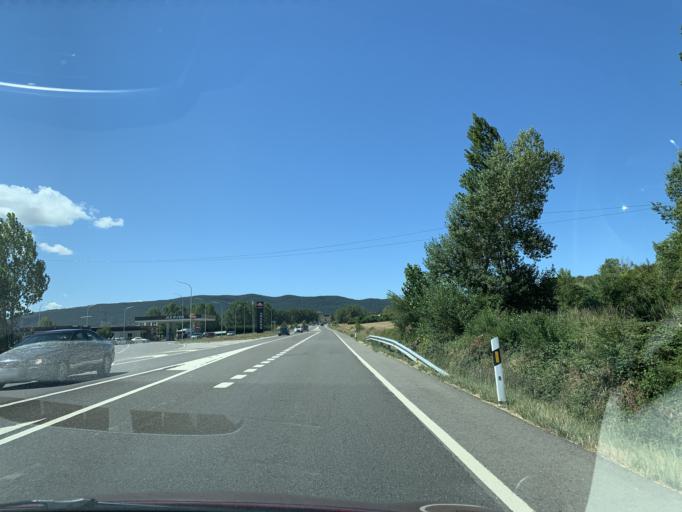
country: ES
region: Aragon
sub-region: Provincia de Huesca
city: Sabinanigo
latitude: 42.5410
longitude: -0.3545
